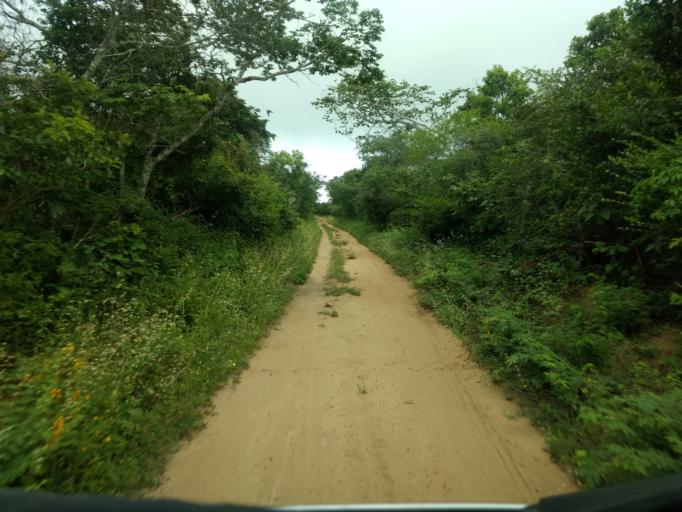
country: BR
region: Ceara
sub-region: Crateus
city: Crateus
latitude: -5.1617
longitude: -40.9242
